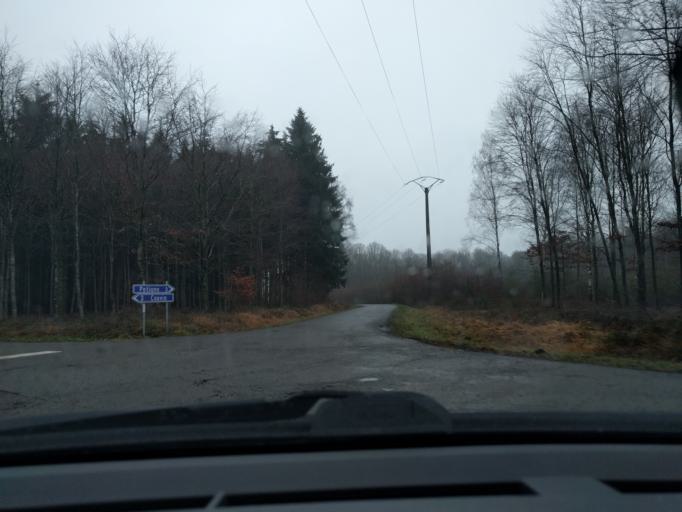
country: BE
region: Wallonia
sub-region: Province de Namur
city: Couvin
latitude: 50.0433
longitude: 4.5347
